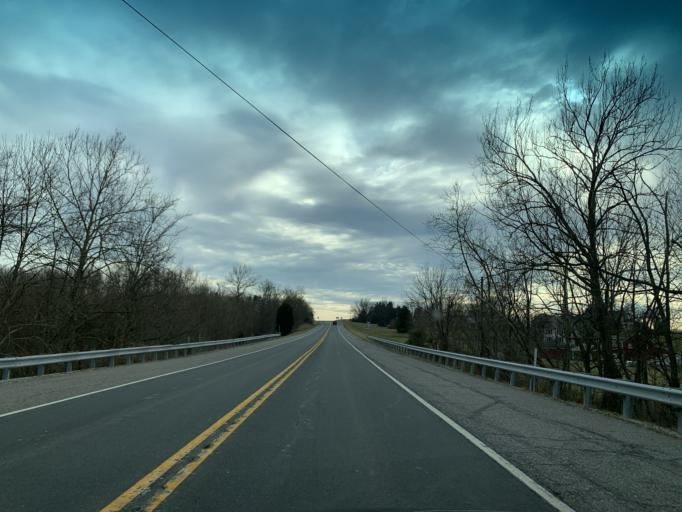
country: US
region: Maryland
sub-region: Washington County
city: Boonsboro
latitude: 39.4959
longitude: -77.6460
